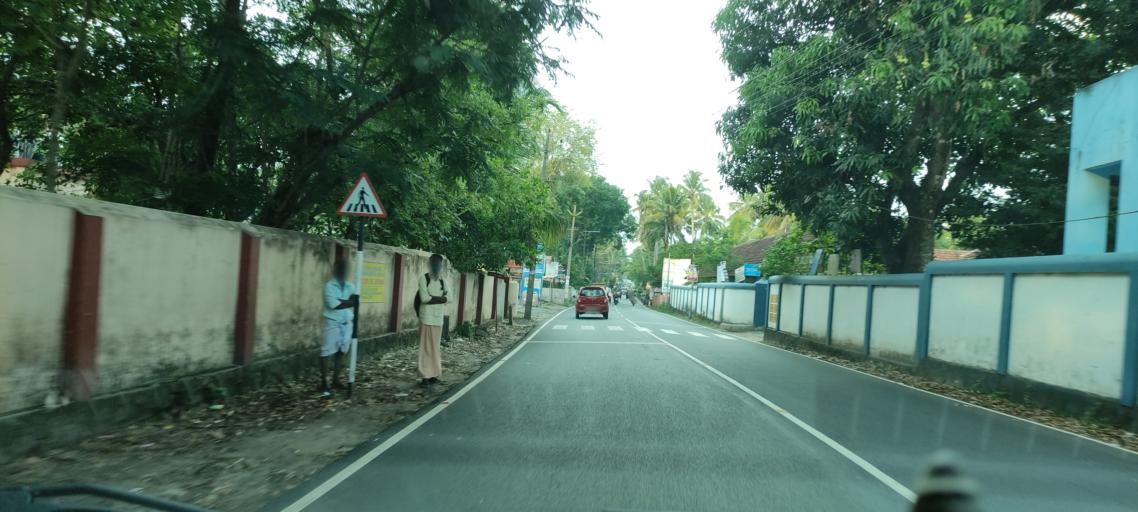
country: IN
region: Kerala
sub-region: Alappuzha
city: Kutiatodu
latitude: 9.8336
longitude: 76.3342
